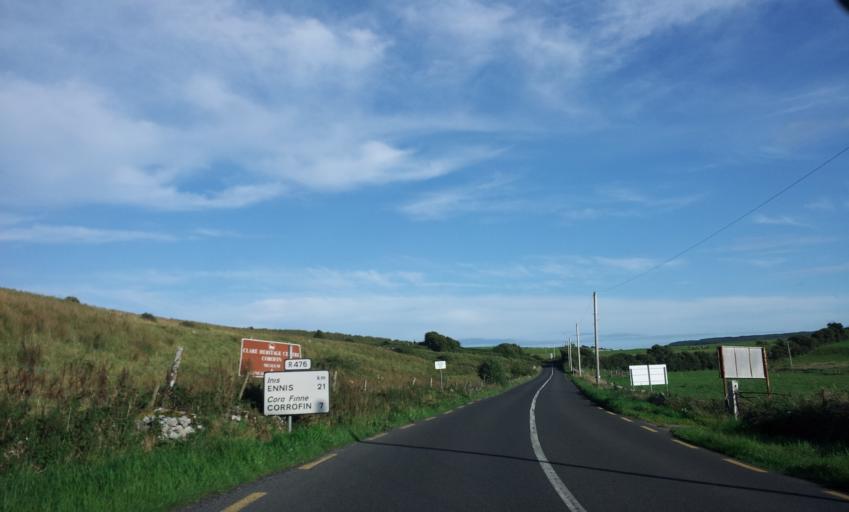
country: IE
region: Munster
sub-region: An Clar
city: Ennis
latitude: 52.9869
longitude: -9.1395
